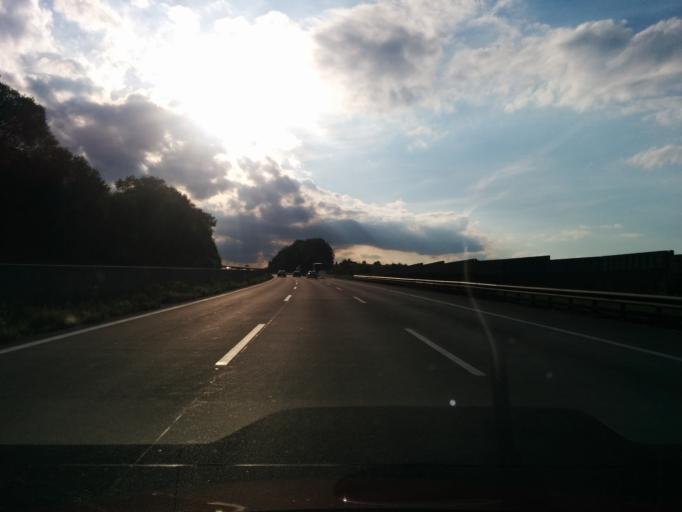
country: AT
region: Lower Austria
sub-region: Politischer Bezirk Amstetten
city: Amstetten
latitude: 48.1471
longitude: 14.9066
